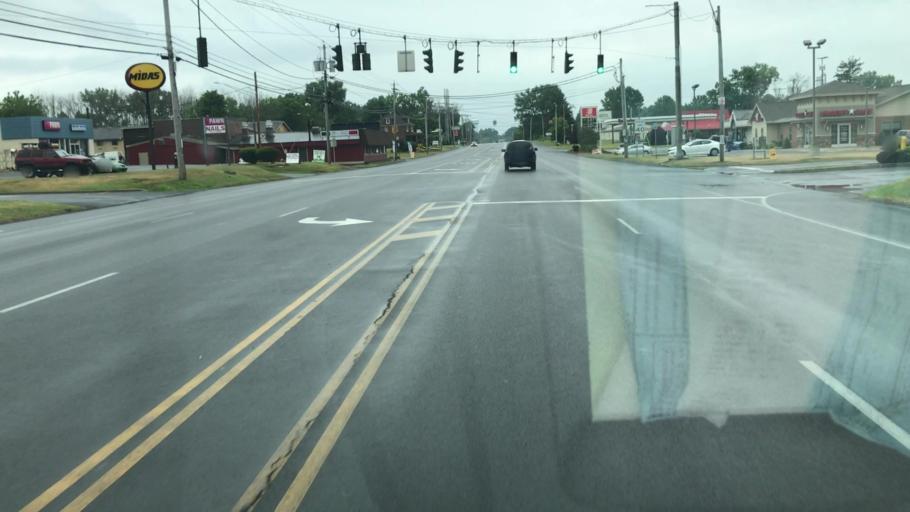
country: US
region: New York
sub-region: Onondaga County
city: Liverpool
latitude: 43.1288
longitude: -76.2190
